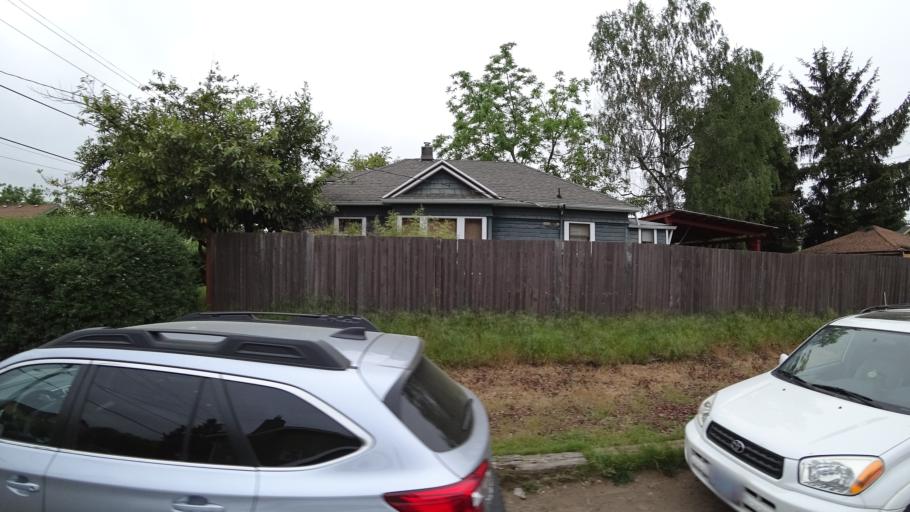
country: US
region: Oregon
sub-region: Multnomah County
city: Portland
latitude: 45.5577
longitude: -122.6376
